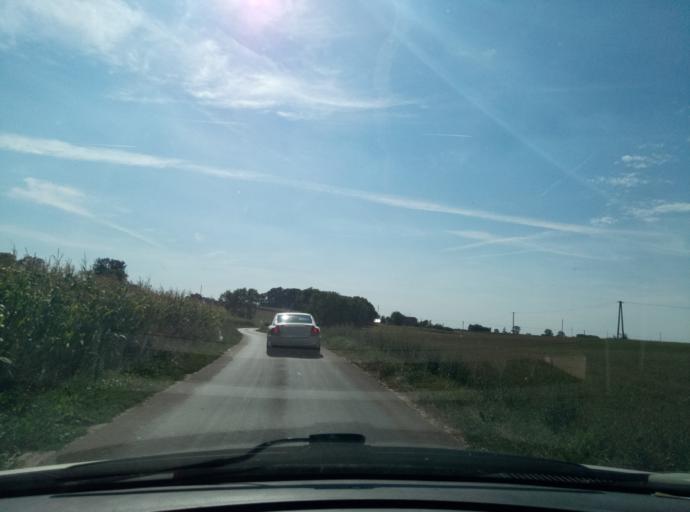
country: PL
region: Kujawsko-Pomorskie
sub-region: Powiat brodnicki
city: Jablonowo Pomorskie
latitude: 53.4031
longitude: 19.2335
